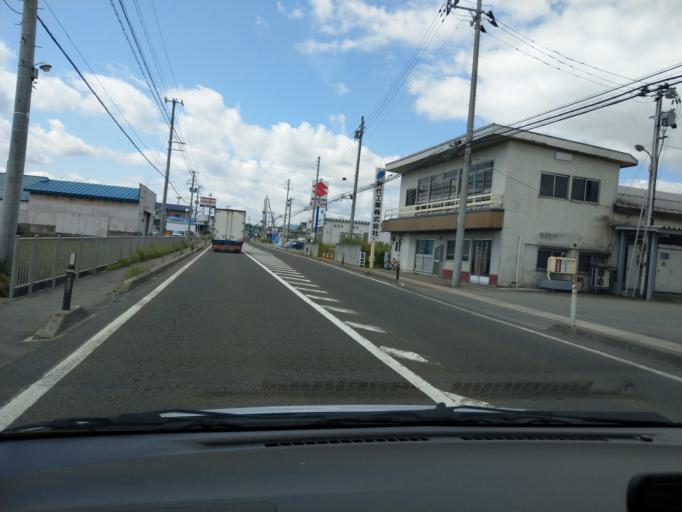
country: JP
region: Akita
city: Yuzawa
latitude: 39.1902
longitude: 140.5017
